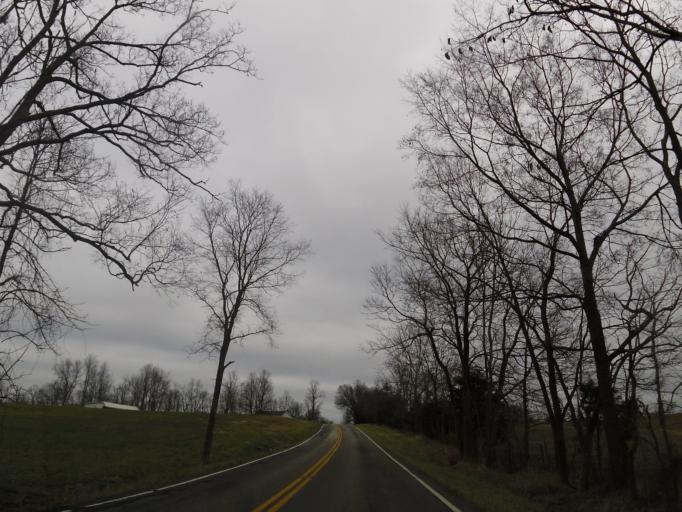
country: US
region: Kentucky
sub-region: Henry County
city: Eminence
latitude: 38.3438
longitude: -85.0474
